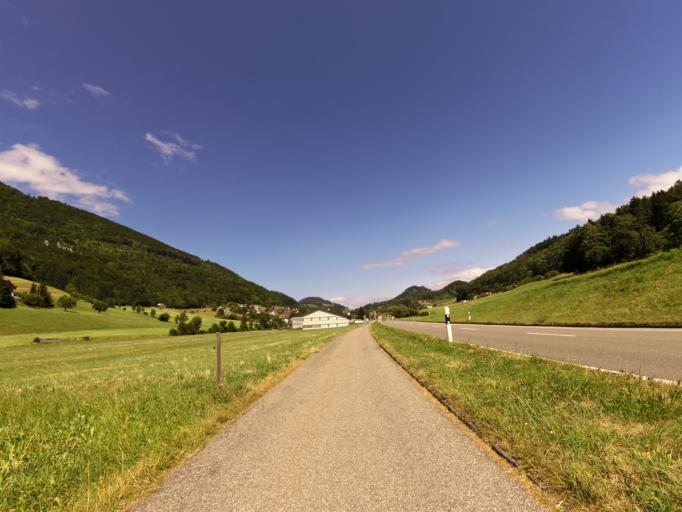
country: CH
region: Solothurn
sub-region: Bezirk Gaeu
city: Oberbuchsiten
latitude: 47.3308
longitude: 7.7420
